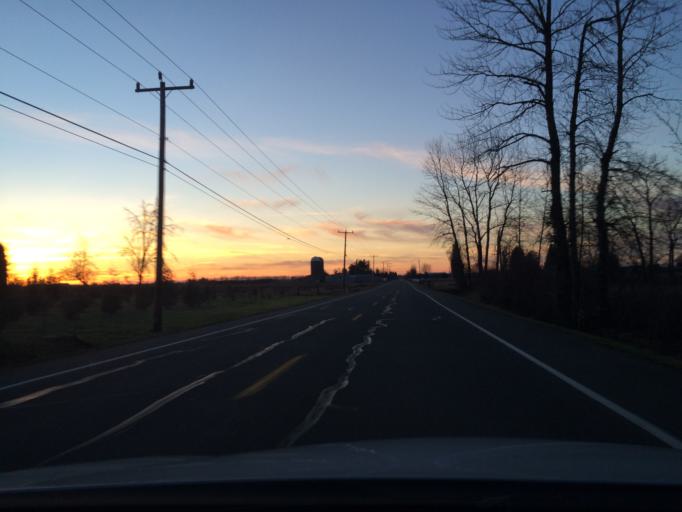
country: US
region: Washington
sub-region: Whatcom County
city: Everson
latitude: 48.9419
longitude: -122.3735
